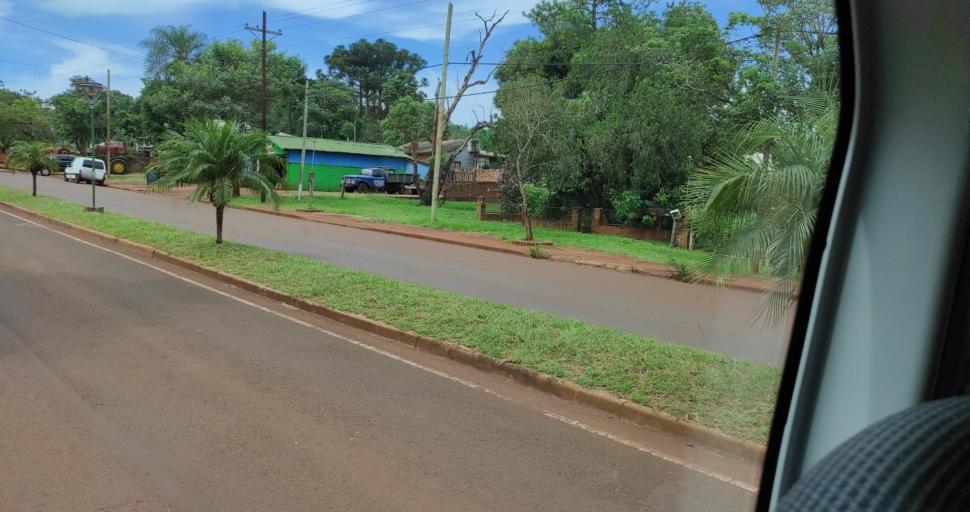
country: AR
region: Misiones
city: El Alcazar
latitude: -26.7086
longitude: -54.8167
